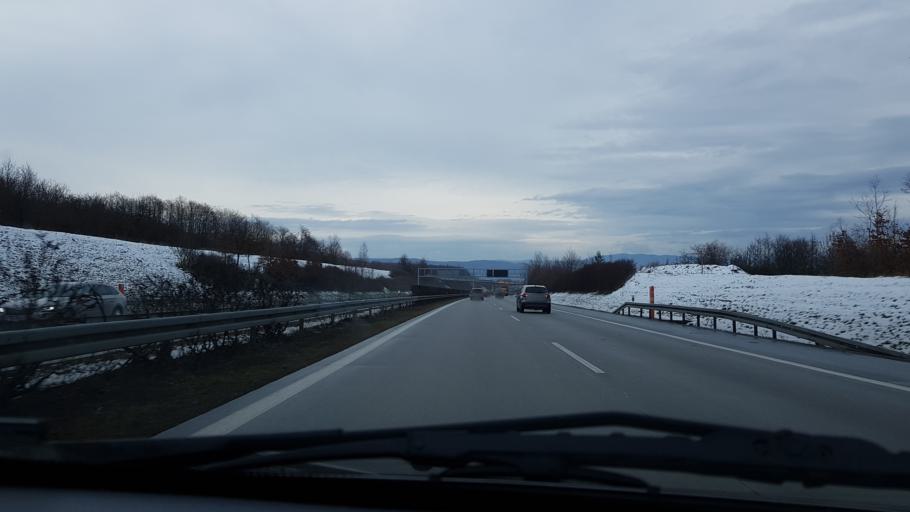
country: CZ
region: Olomoucky
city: Dolni Ujezd
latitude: 49.5572
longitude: 17.5208
